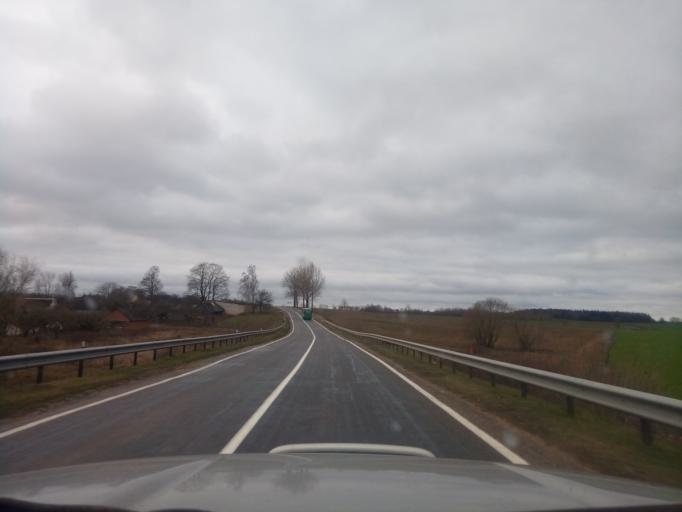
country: BY
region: Minsk
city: Kapyl'
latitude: 53.1788
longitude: 27.1684
